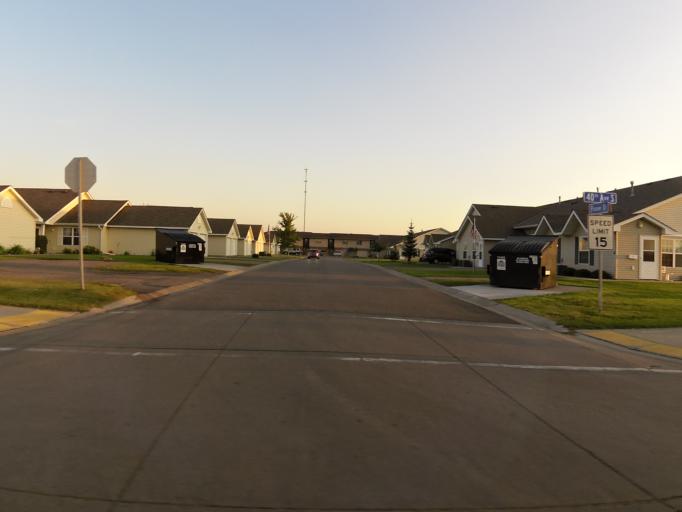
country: US
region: North Dakota
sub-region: Grand Forks County
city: Grand Forks
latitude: 47.8821
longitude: -97.0492
